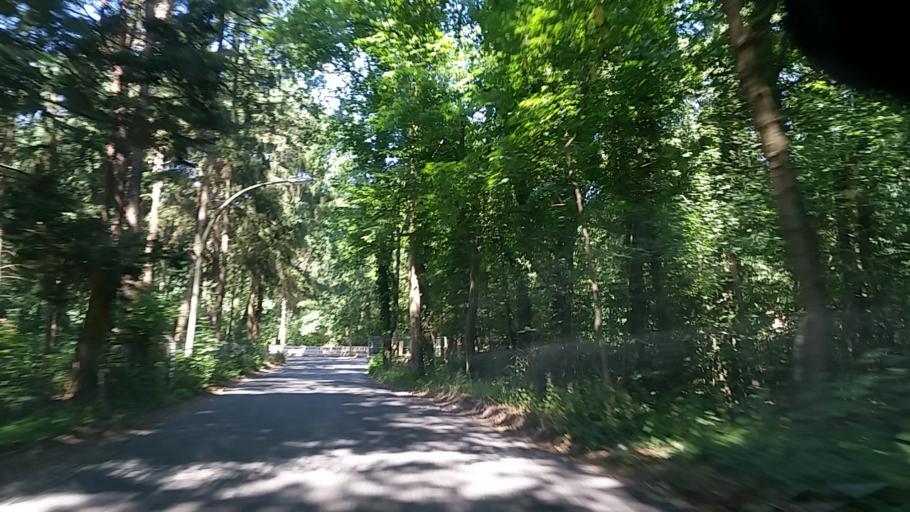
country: DE
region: Schleswig-Holstein
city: Wedel
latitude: 53.5701
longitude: 9.7642
